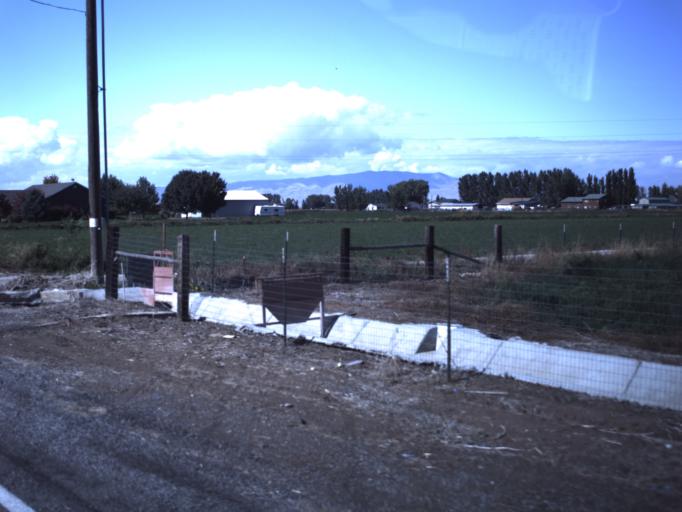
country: US
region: Utah
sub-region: Utah County
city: Benjamin
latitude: 40.1148
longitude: -111.7070
